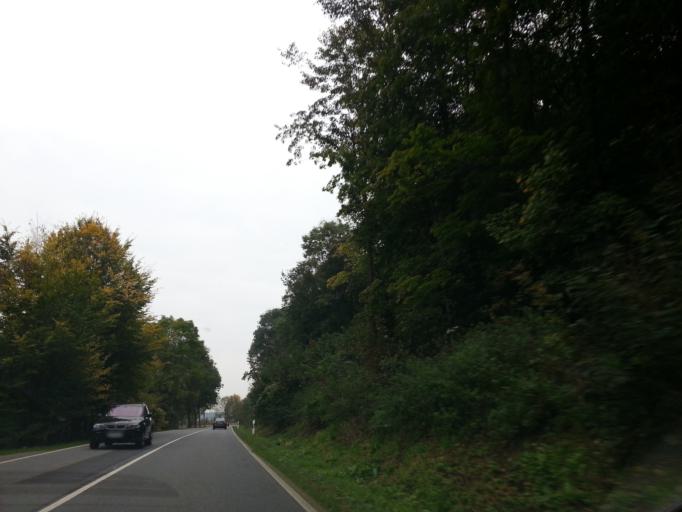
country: DE
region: Saxony
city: Klipphausen
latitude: 51.1309
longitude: 13.5219
